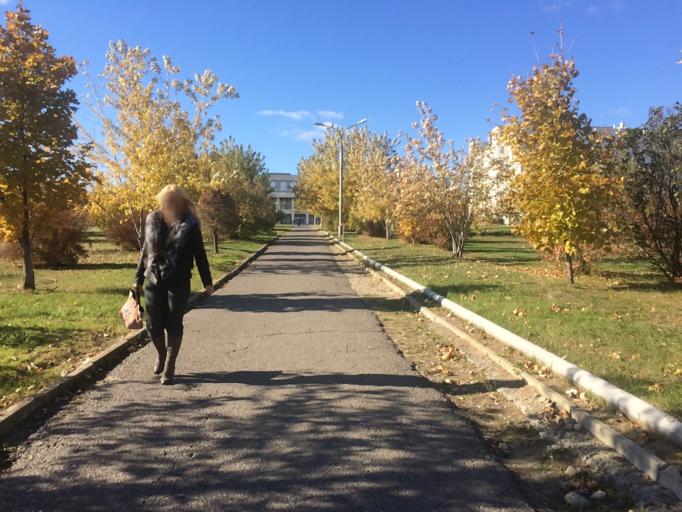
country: RU
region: Volgograd
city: Volgograd
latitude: 48.6413
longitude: 44.4262
